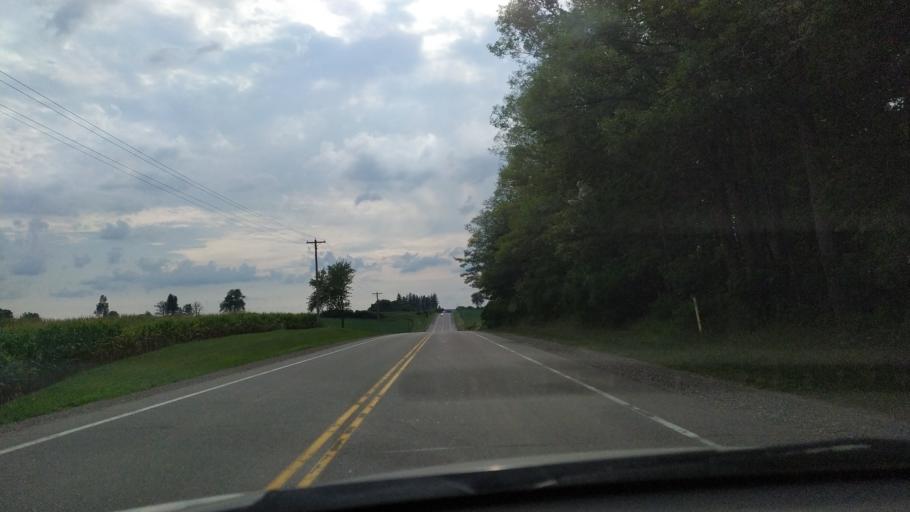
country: CA
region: Ontario
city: Kitchener
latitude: 43.3558
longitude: -80.4940
